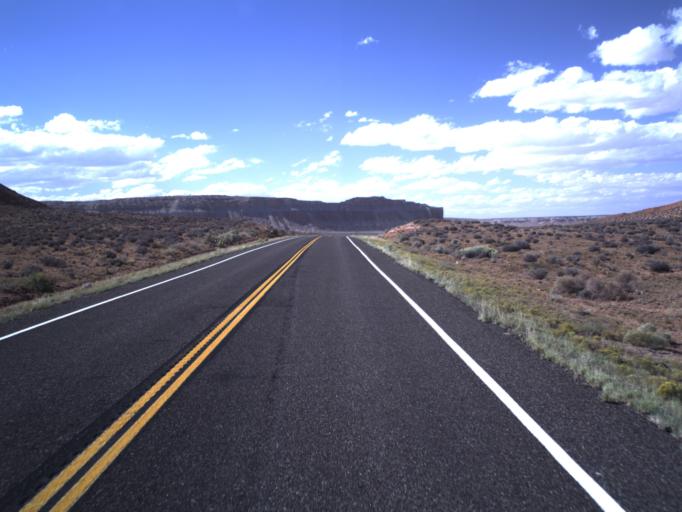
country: US
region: Utah
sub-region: Wayne County
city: Loa
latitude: 38.1463
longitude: -110.6154
